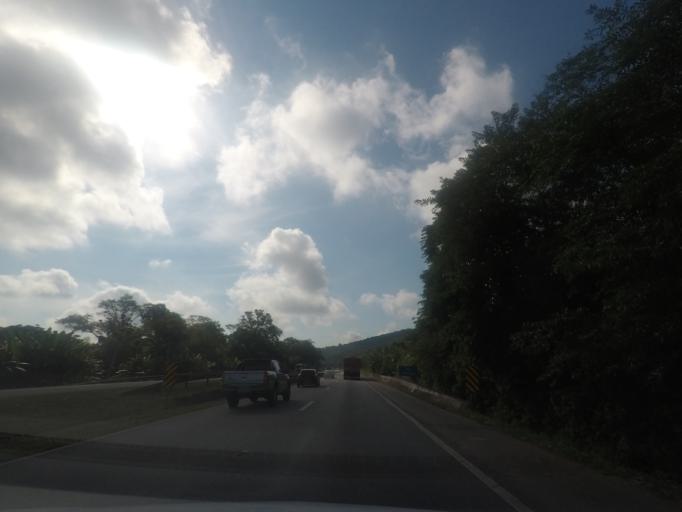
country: BR
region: Parana
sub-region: Antonina
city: Antonina
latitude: -25.5461
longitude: -48.7862
